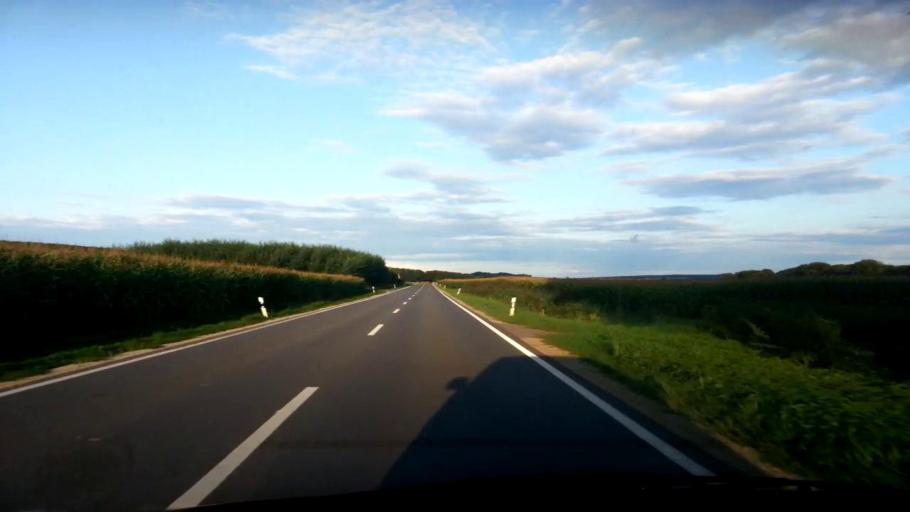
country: DE
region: Bavaria
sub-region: Upper Franconia
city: Burgwindheim
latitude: 49.8249
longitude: 10.6219
